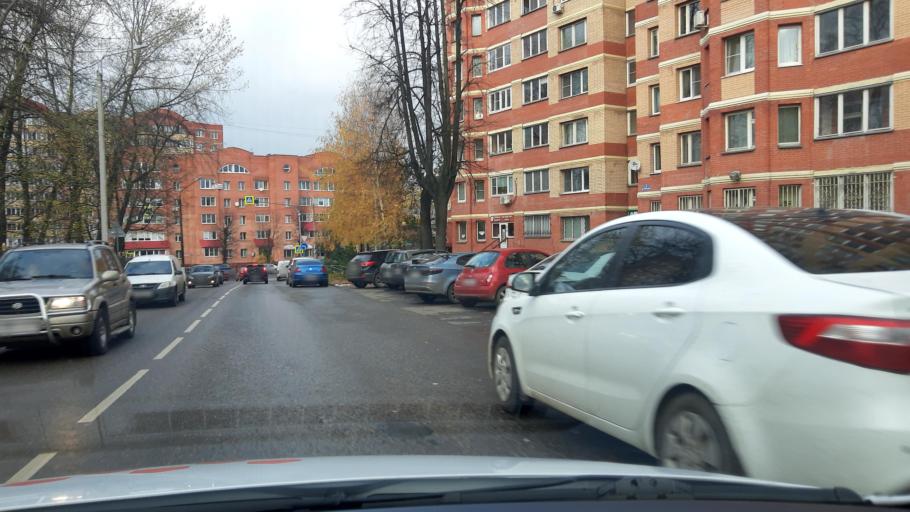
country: RU
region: Moskovskaya
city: Noginsk
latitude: 55.8513
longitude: 38.4310
